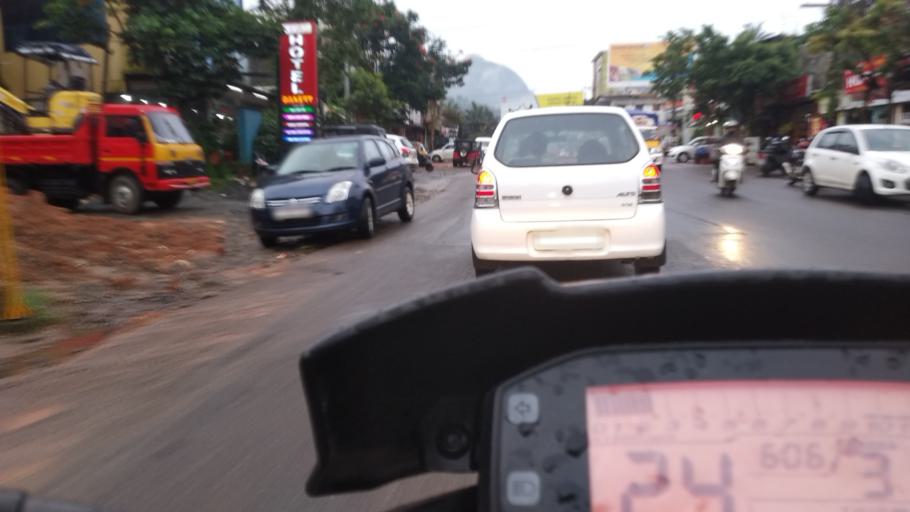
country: IN
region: Kerala
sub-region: Idukki
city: Munnar
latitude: 10.0147
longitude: 76.9499
